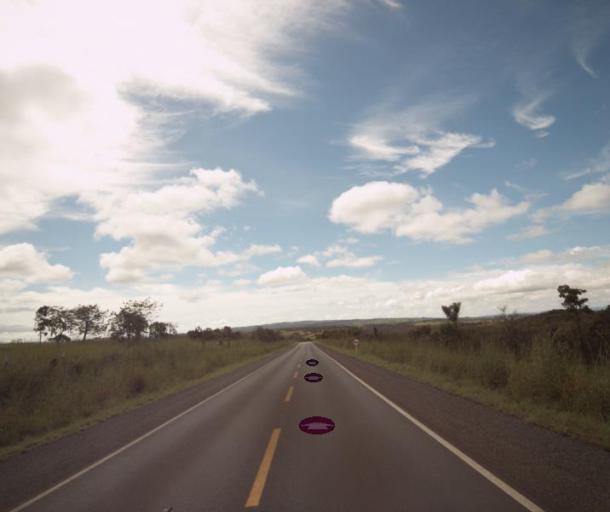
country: BR
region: Goias
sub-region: Padre Bernardo
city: Padre Bernardo
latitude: -15.2154
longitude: -48.5973
